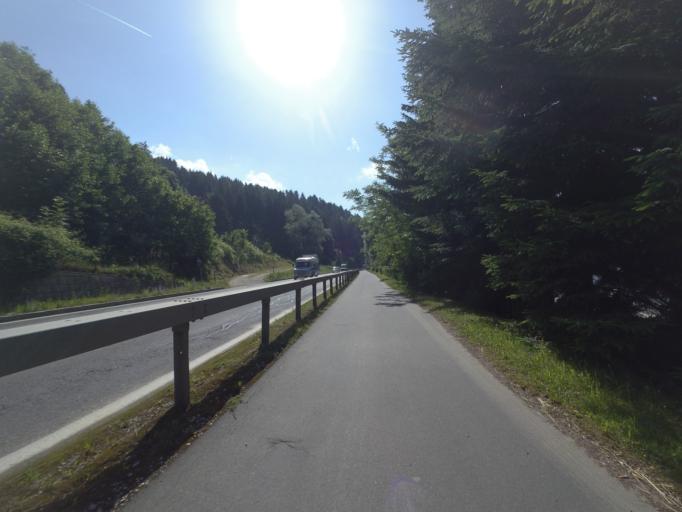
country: AT
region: Carinthia
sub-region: Politischer Bezirk Spittal an der Drau
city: Seeboden
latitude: 46.8153
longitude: 13.5379
